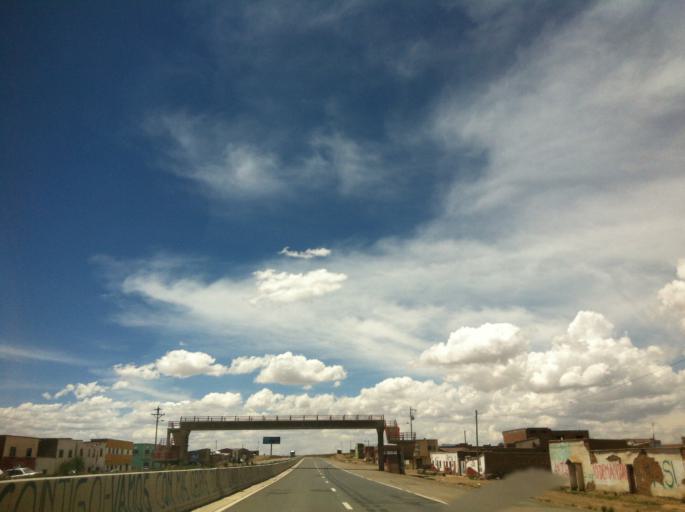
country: BO
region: La Paz
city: Patacamaya
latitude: -17.0946
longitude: -68.0055
